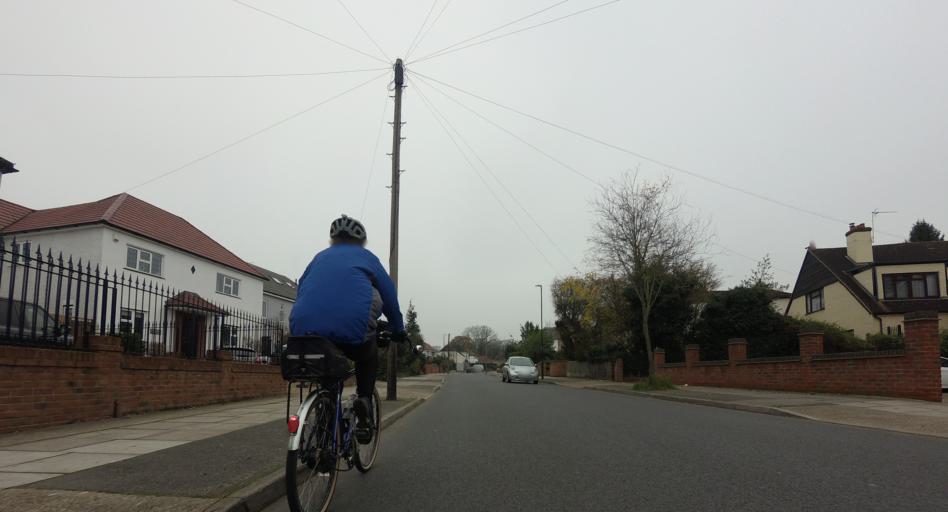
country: GB
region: England
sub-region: Greater London
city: Bexley
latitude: 51.4332
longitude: 0.1658
